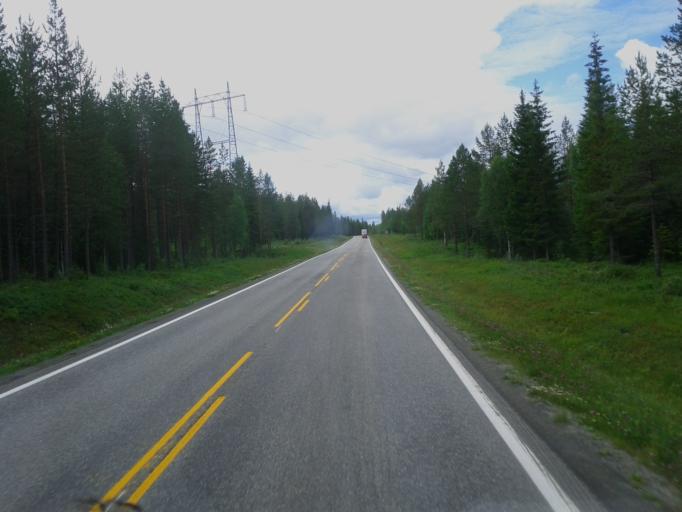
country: NO
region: Nord-Trondelag
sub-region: Hoylandet
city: Hoylandet
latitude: 64.6522
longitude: 12.6471
